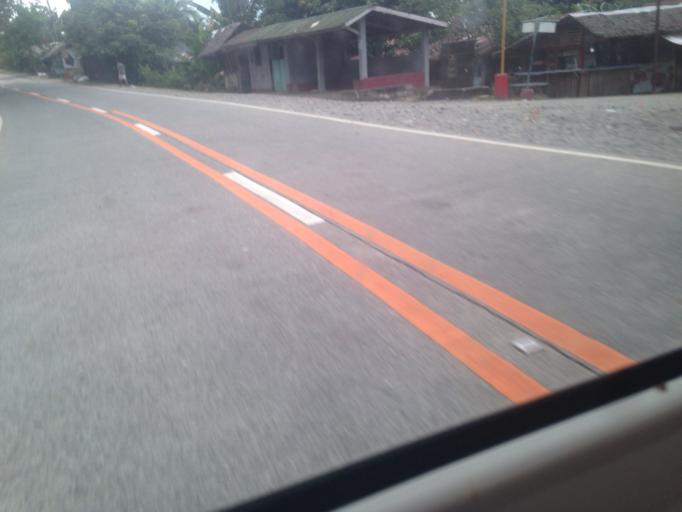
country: PH
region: Mimaropa
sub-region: Province of Mindoro Oriental
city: Saaban
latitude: 13.1106
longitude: 121.3166
